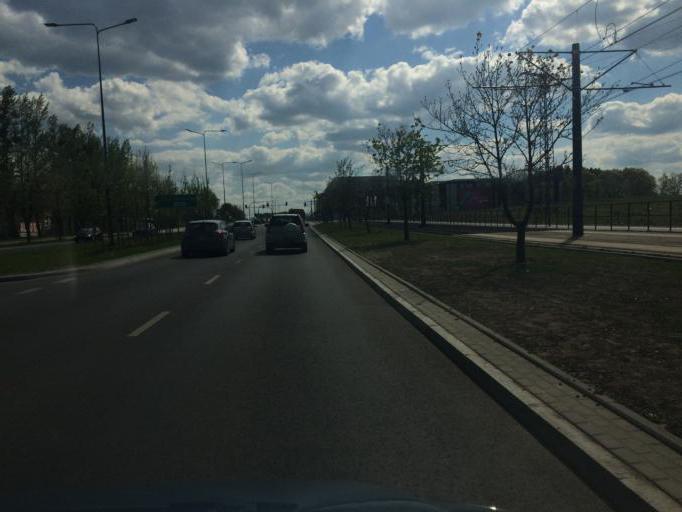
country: PL
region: Warmian-Masurian Voivodeship
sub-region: Powiat olsztynski
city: Olsztyn
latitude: 53.7578
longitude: 20.4865
